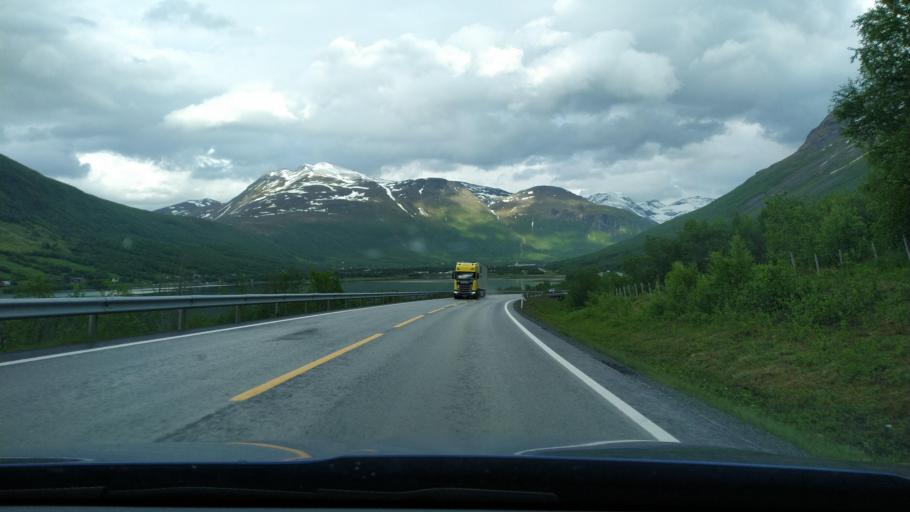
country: NO
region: Troms
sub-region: Balsfjord
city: Storsteinnes
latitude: 69.2153
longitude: 19.5002
